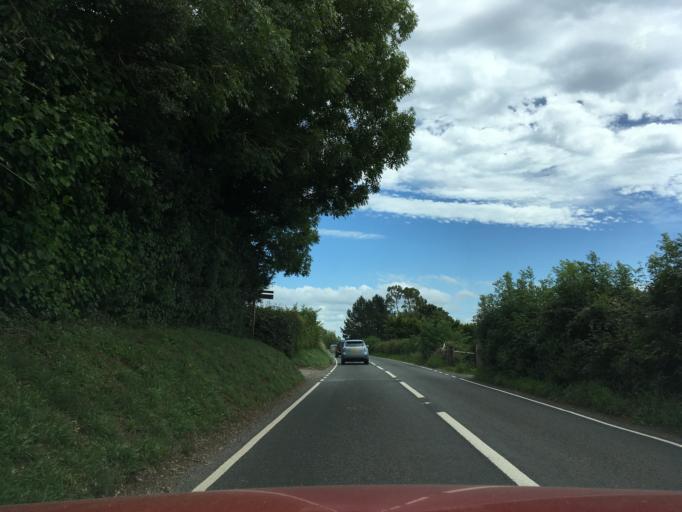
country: GB
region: England
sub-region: Somerset
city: Bradley Cross
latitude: 51.2406
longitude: -2.7283
